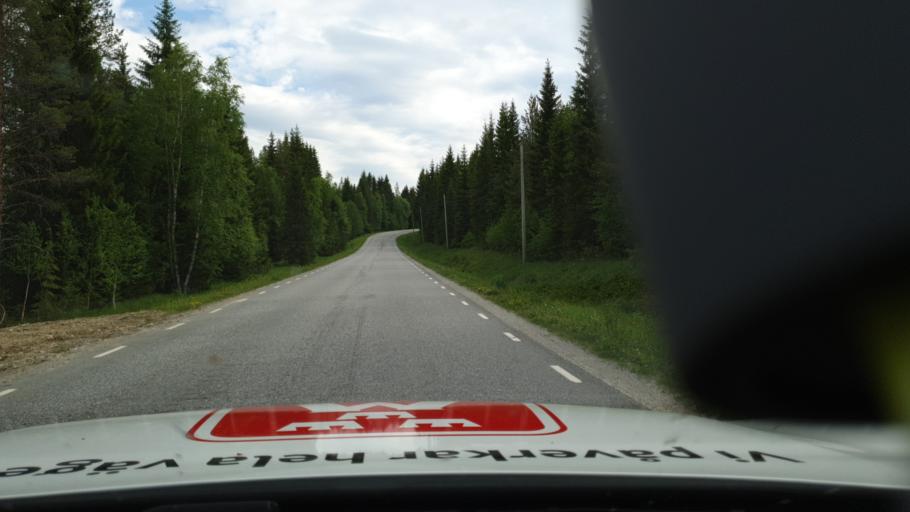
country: SE
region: Jaemtland
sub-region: Braecke Kommun
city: Braecke
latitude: 63.0544
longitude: 15.3257
